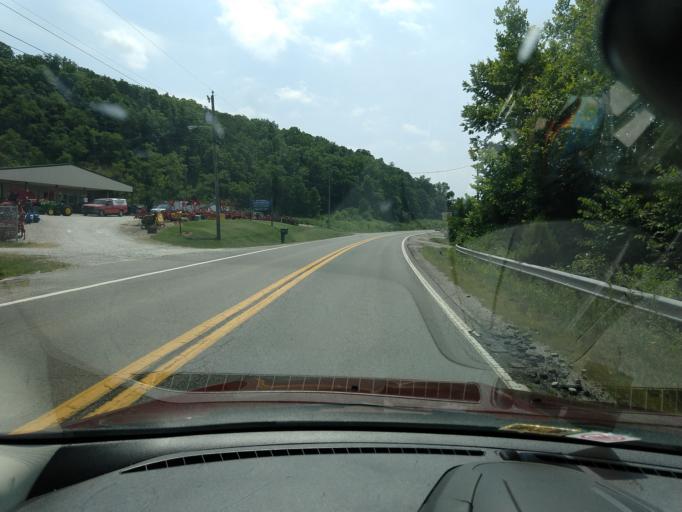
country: US
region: West Virginia
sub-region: Jackson County
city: Ripley
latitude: 38.8383
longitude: -81.7803
